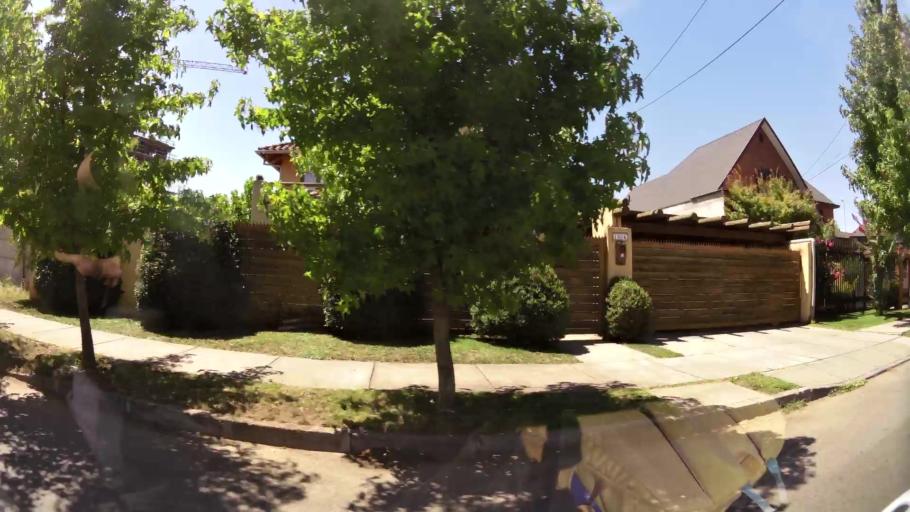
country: CL
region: Maule
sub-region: Provincia de Curico
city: Curico
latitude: -34.9795
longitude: -71.2218
